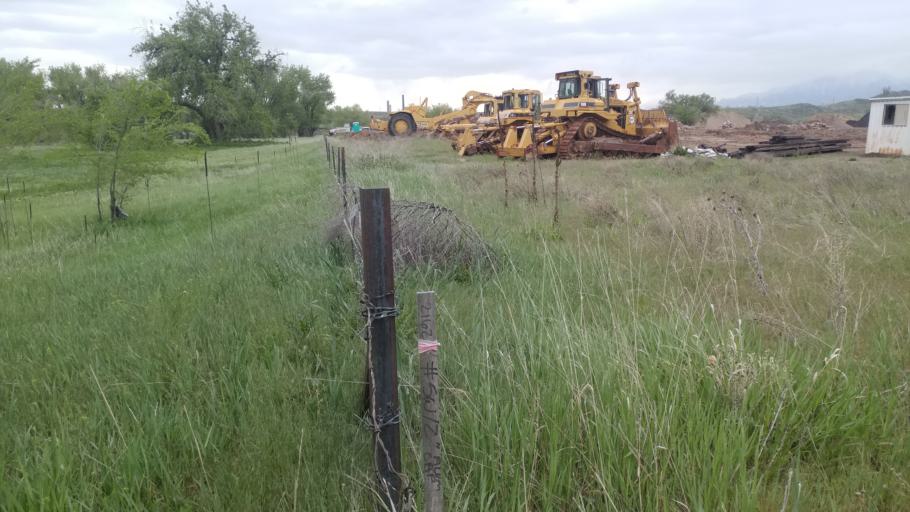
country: US
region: Colorado
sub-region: Boulder County
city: Gunbarrel
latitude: 40.0401
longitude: -105.1992
